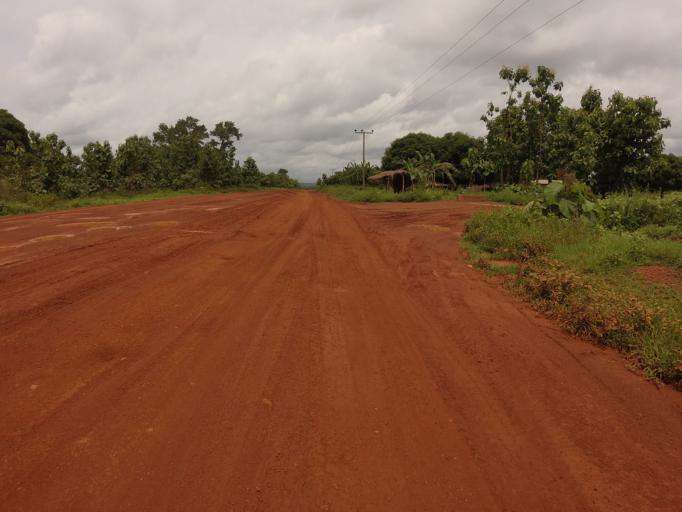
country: GH
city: Kpandae
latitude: 8.4125
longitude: 0.3928
